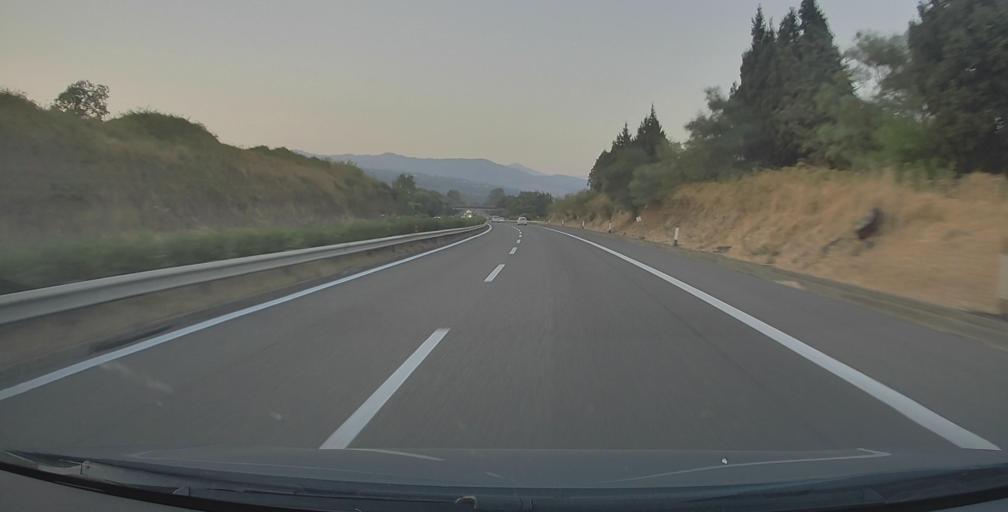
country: IT
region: Sicily
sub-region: Catania
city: Nunziata
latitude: 37.7635
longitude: 15.1828
